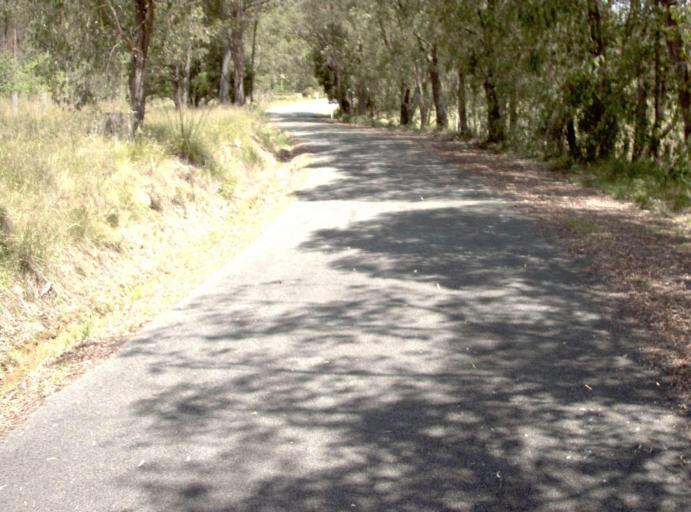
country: AU
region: New South Wales
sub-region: Bombala
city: Bombala
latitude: -37.3983
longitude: 149.0138
